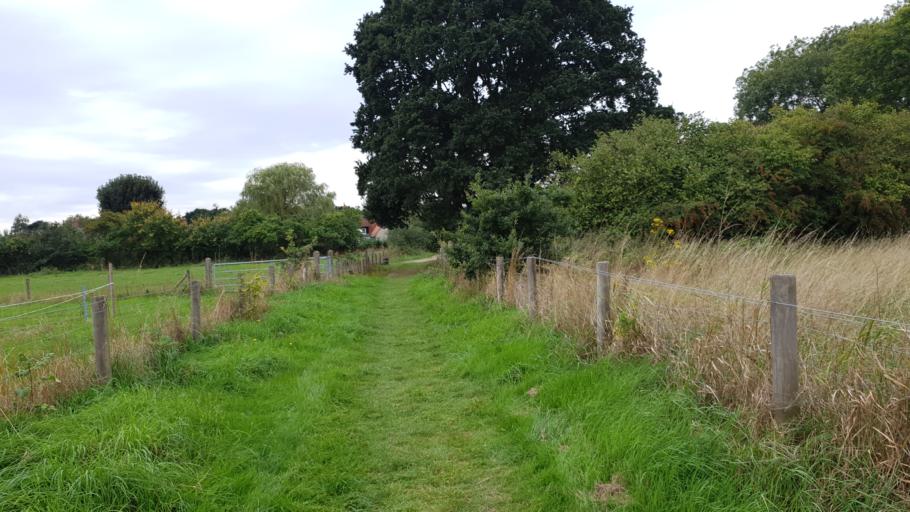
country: GB
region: England
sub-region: Suffolk
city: East Bergholt
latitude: 51.9469
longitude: 0.9981
